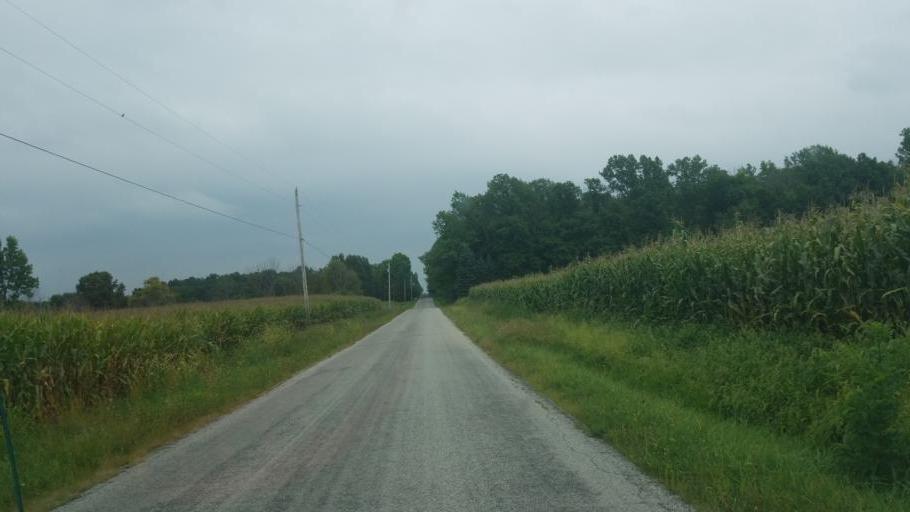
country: US
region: Ohio
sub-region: Medina County
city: Lodi
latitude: 40.9598
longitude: -81.9913
